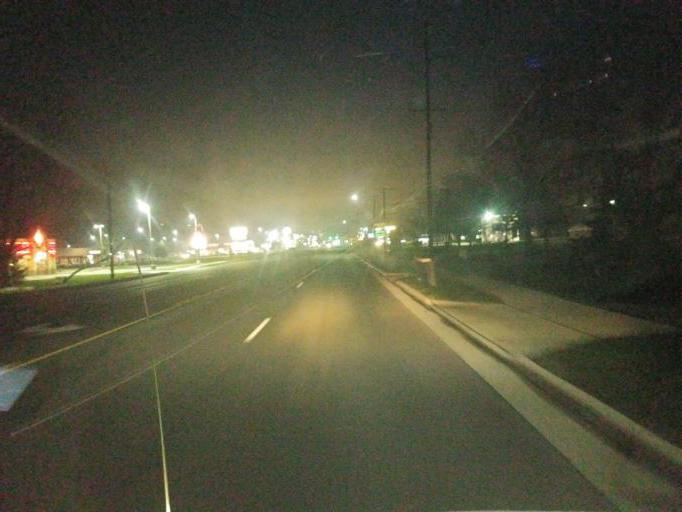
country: US
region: Ohio
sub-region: Williams County
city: Bryan
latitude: 41.4577
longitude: -84.5507
